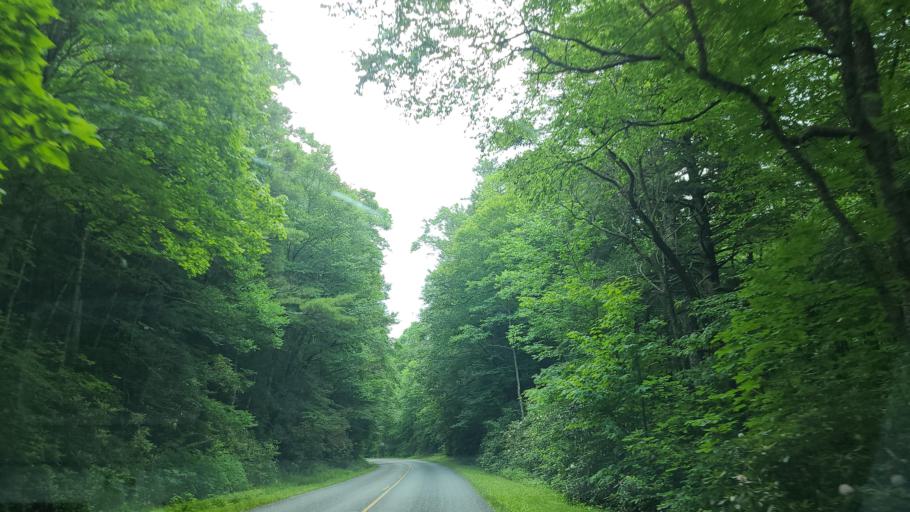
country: US
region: North Carolina
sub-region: Avery County
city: Newland
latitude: 35.9863
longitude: -81.9006
